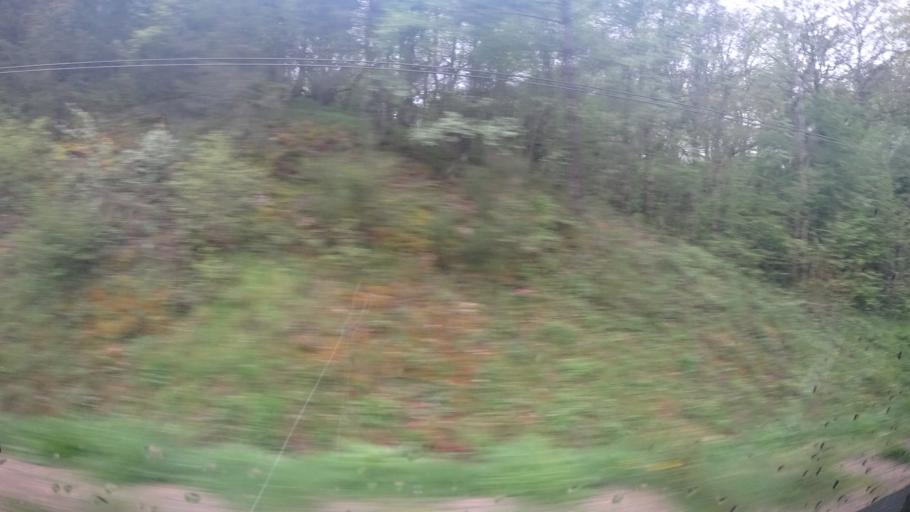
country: FR
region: Midi-Pyrenees
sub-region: Departement de l'Aveyron
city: Laissac
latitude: 44.2716
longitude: 2.8648
